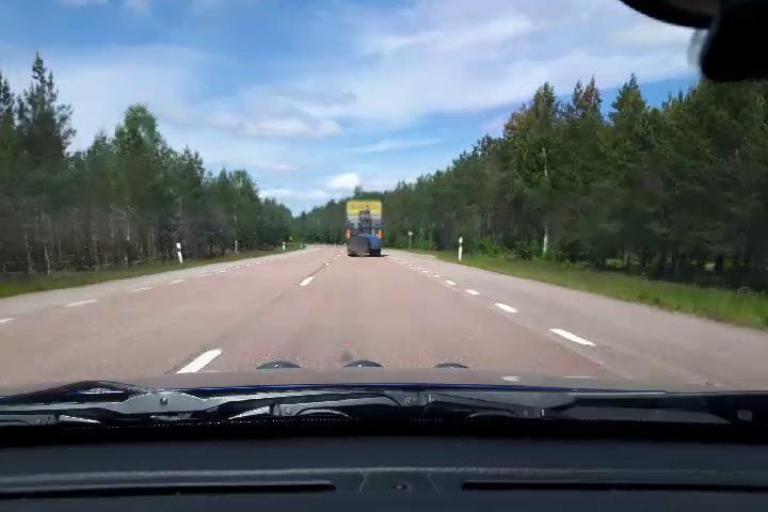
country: SE
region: Uppsala
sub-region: Osthammars Kommun
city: Bjorklinge
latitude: 60.1302
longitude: 17.5095
